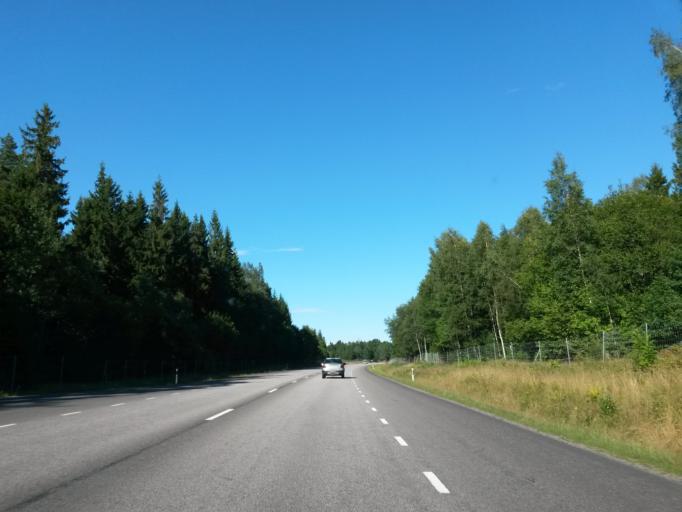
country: SE
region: Vaestra Goetaland
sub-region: Vanersborgs Kommun
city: Vargon
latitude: 58.3007
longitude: 12.5112
